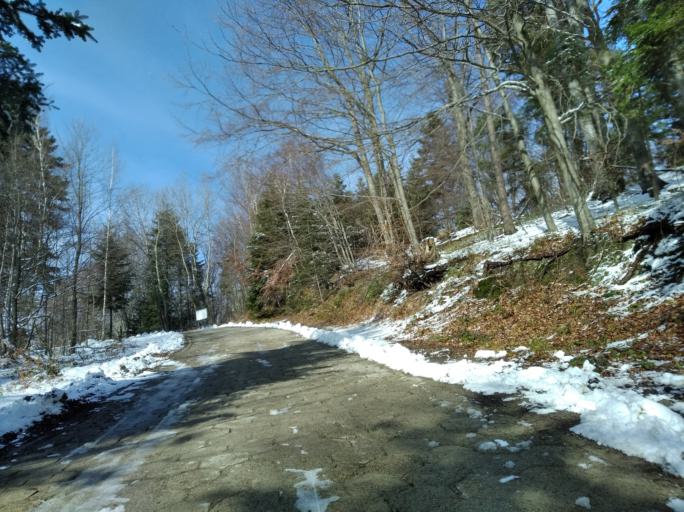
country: PL
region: Subcarpathian Voivodeship
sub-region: Powiat krosnienski
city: Korczyna
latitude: 49.7552
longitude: 21.8149
